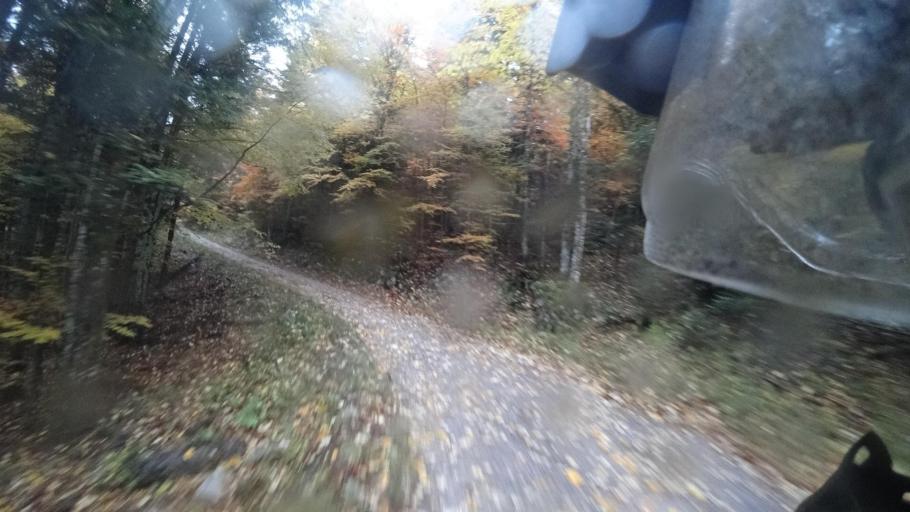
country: HR
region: Primorsko-Goranska
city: Vrbovsko
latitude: 45.2669
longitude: 15.0015
